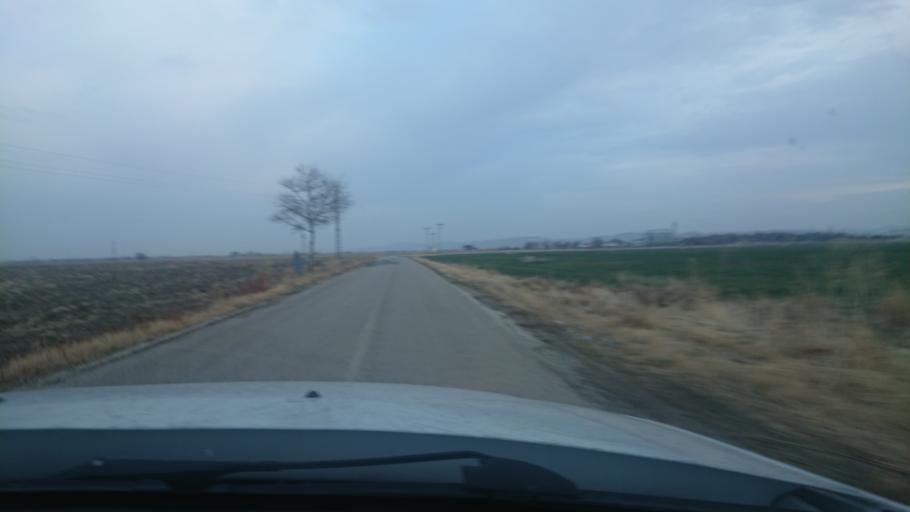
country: TR
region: Aksaray
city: Yesilova
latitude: 38.4482
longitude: 33.8350
